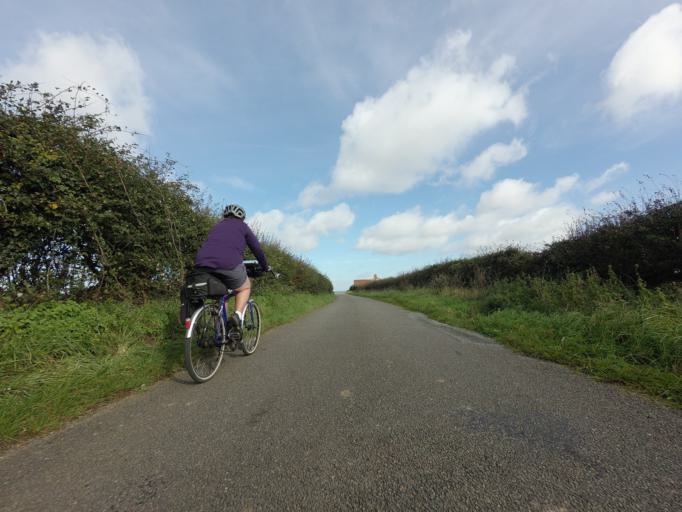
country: GB
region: England
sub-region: Norfolk
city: Wells-next-the-Sea
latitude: 52.9327
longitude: 0.7261
